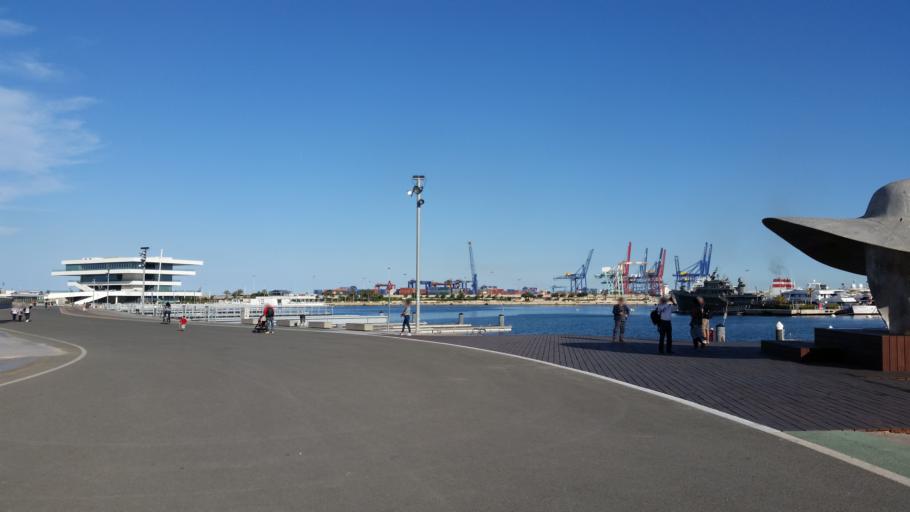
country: ES
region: Valencia
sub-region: Provincia de Valencia
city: Alboraya
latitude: 39.4618
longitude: -0.3294
